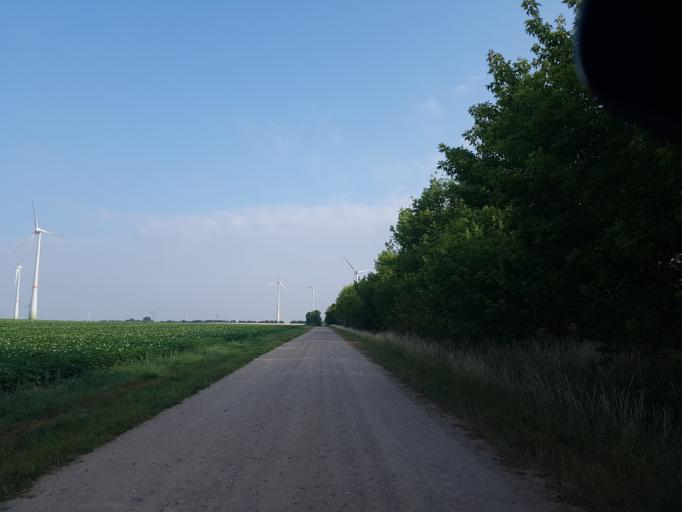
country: DE
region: Saxony-Anhalt
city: Kropstadt
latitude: 51.9876
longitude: 12.8204
